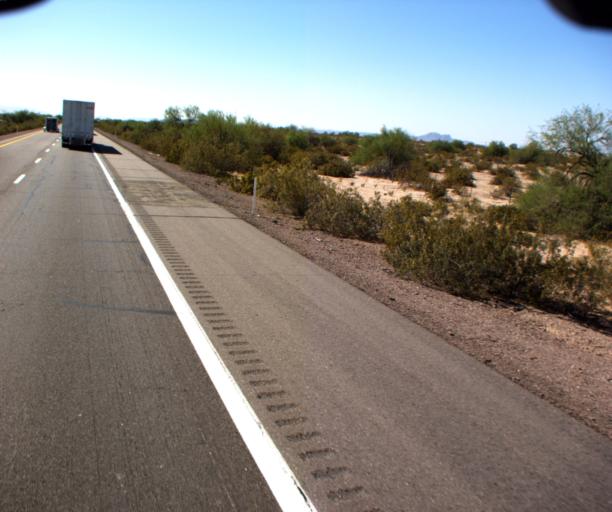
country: US
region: Arizona
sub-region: Yuma County
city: Wellton
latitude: 32.7069
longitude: -113.8665
